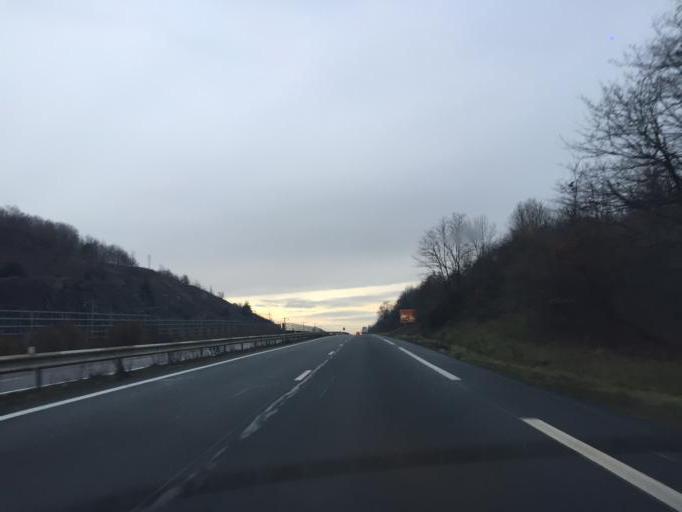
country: FR
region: Bourgogne
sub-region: Departement de Saone-et-Loire
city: Cluny
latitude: 46.3779
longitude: 4.6709
